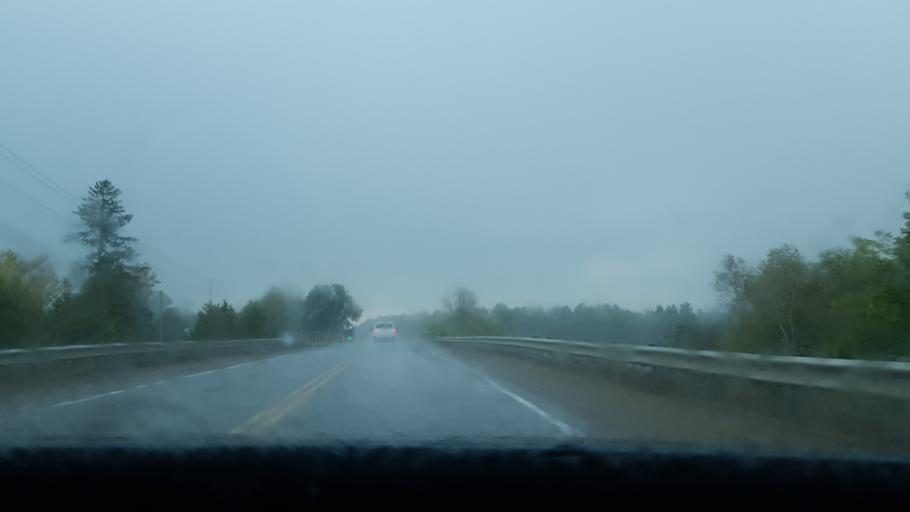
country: CA
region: Ontario
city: Omemee
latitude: 44.3419
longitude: -78.5430
